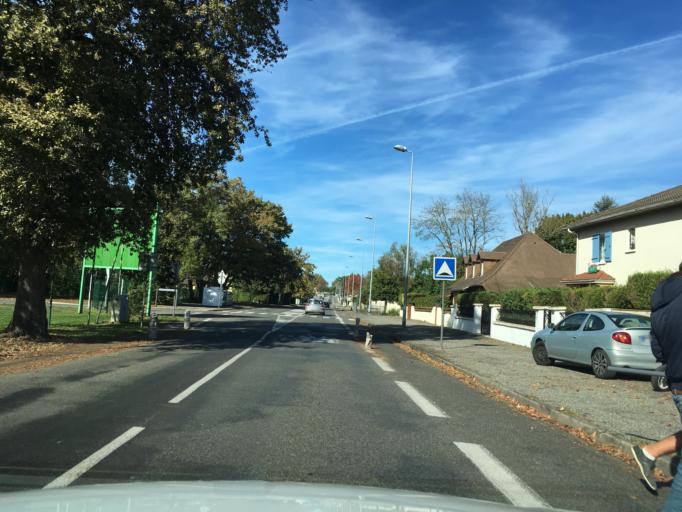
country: FR
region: Aquitaine
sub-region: Departement des Pyrenees-Atlantiques
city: Pau
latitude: 43.3258
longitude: -0.3607
